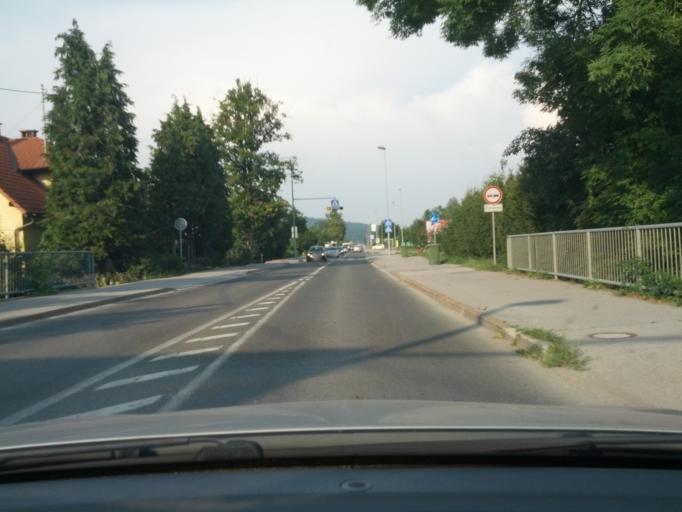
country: SI
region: Horjul
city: Horjul
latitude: 45.9945
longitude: 14.3295
